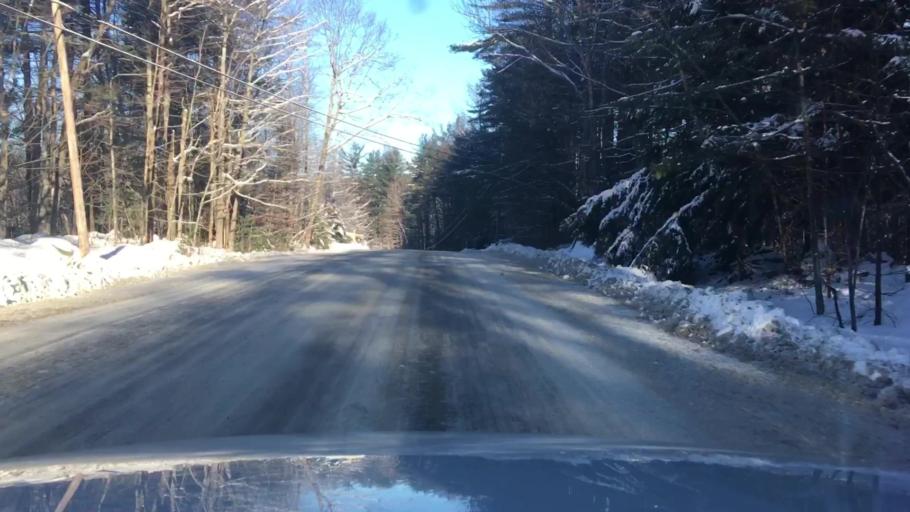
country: US
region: Maine
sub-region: Kennebec County
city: Readfield
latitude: 44.4173
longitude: -69.9219
